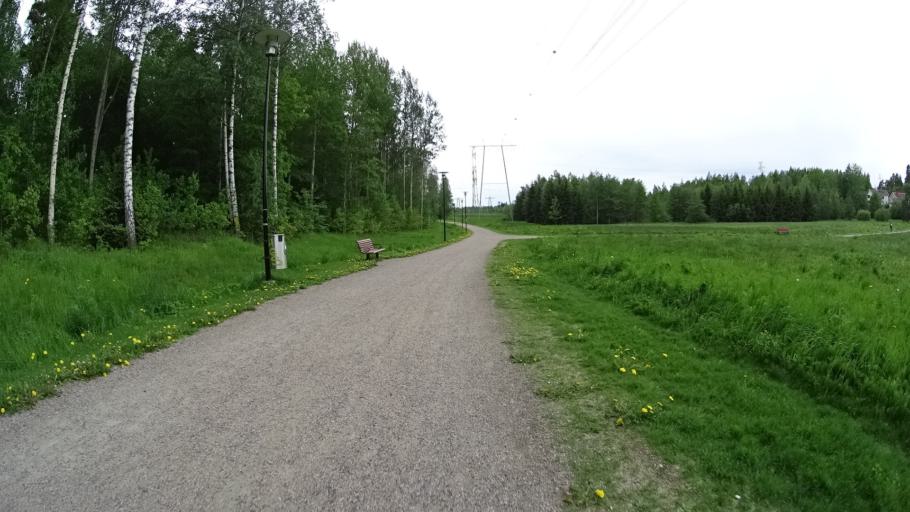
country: FI
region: Uusimaa
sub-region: Helsinki
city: Vantaa
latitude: 60.2818
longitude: 25.0578
